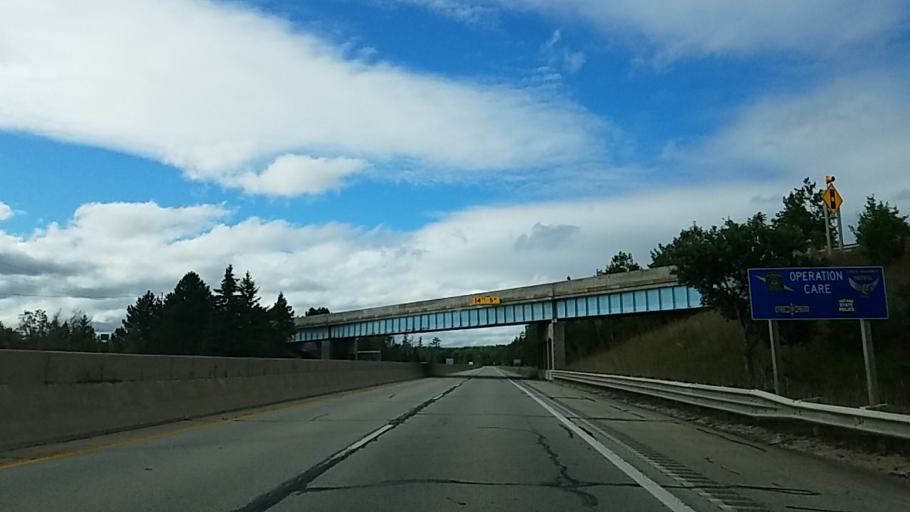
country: US
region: Michigan
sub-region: Mackinac County
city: Saint Ignace
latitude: 45.7731
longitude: -84.7345
